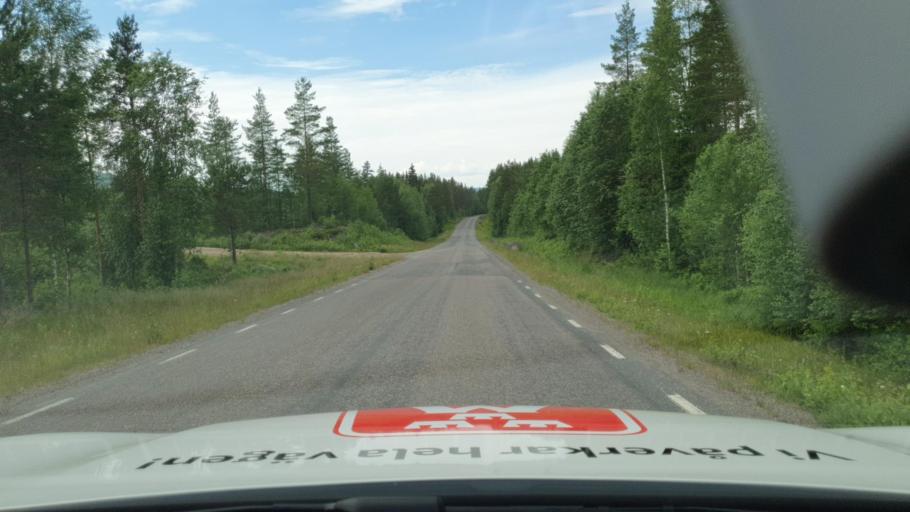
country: NO
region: Hedmark
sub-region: Grue
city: Kirkenaer
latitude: 60.6834
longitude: 12.6469
